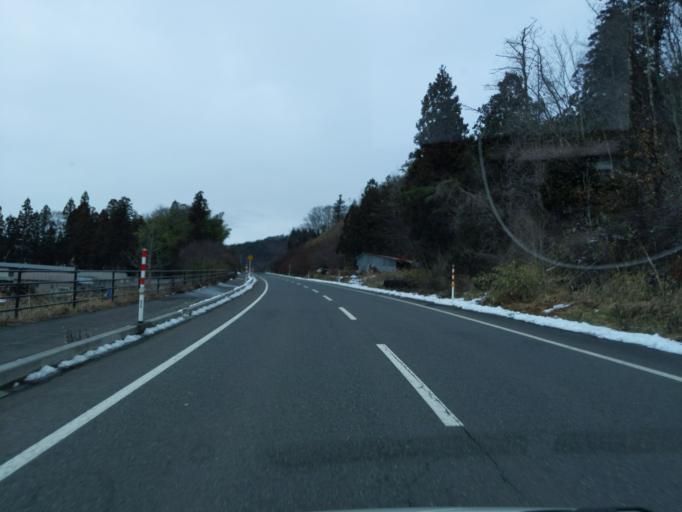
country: JP
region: Iwate
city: Mizusawa
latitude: 39.1739
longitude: 141.2650
